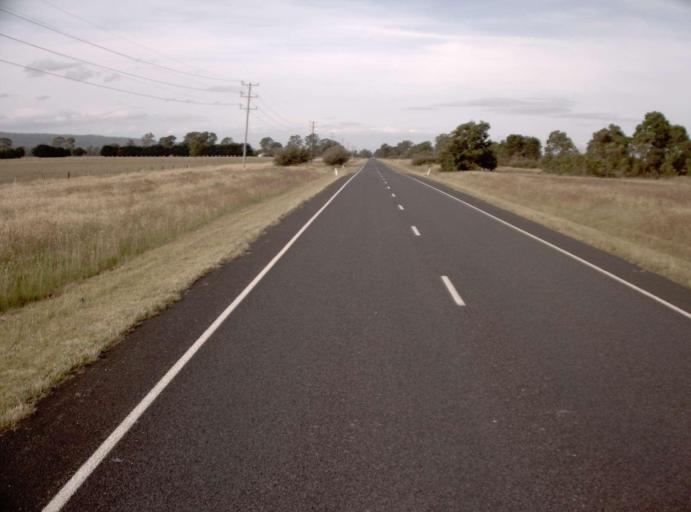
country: AU
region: Victoria
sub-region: Latrobe
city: Traralgon
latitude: -38.0843
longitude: 146.6056
